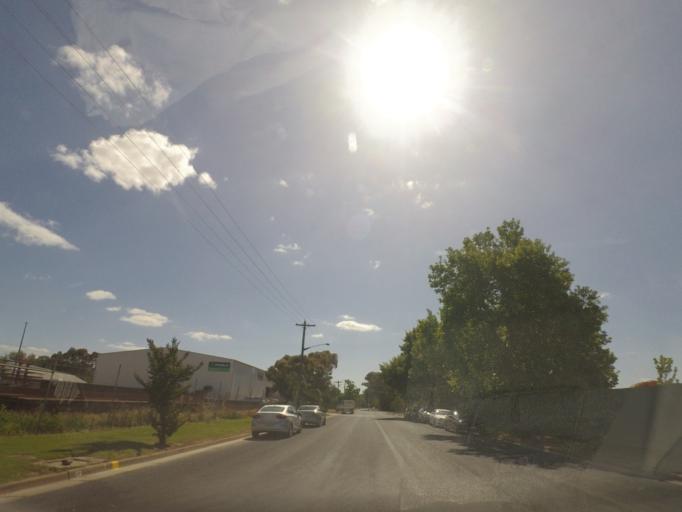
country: AU
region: New South Wales
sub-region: Albury Municipality
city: South Albury
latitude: -36.0931
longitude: 146.9151
